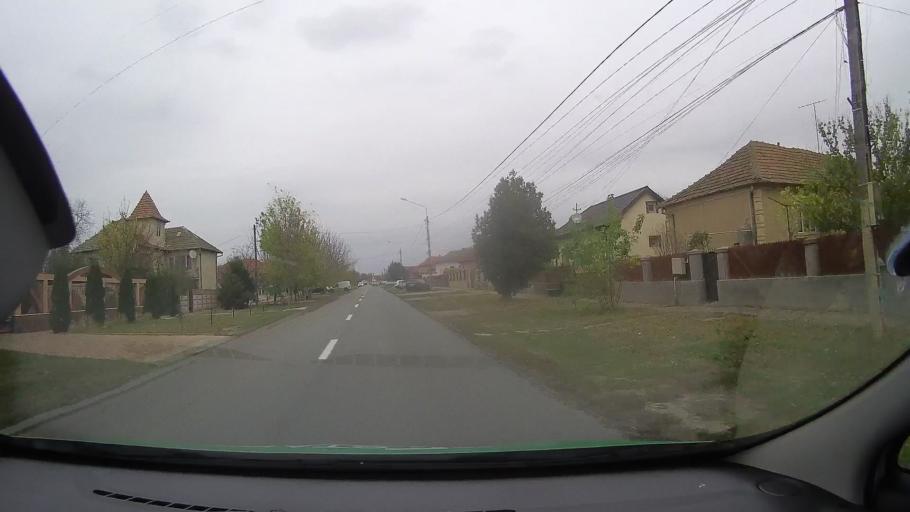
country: RO
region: Constanta
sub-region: Comuna Mihail Kogalniceanu
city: Mihail Kogalniceanu
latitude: 44.3750
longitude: 28.4647
